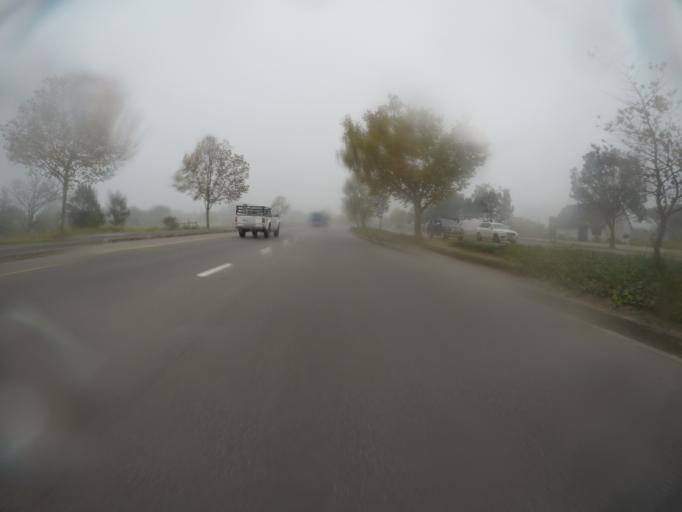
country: ZA
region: Western Cape
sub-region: Eden District Municipality
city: George
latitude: -33.9808
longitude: 22.4409
